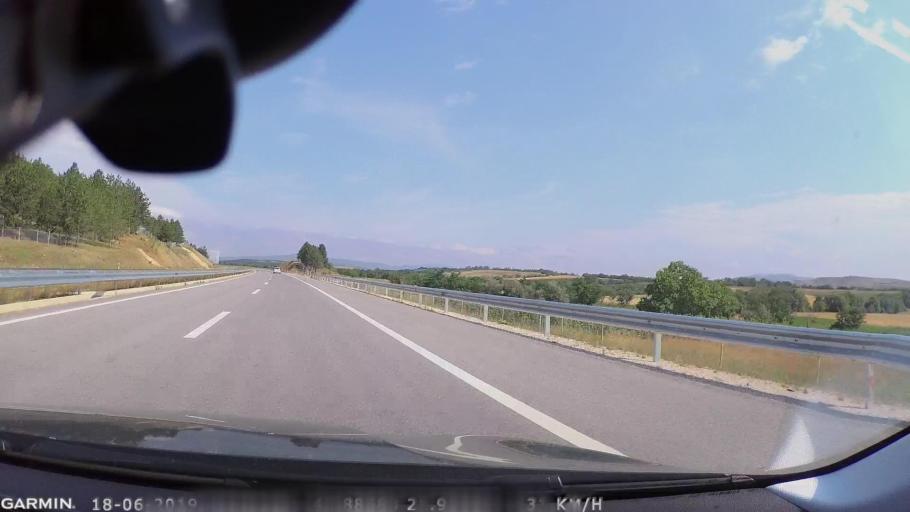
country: MK
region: Sveti Nikole
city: Sveti Nikole
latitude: 41.8877
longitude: 21.9317
